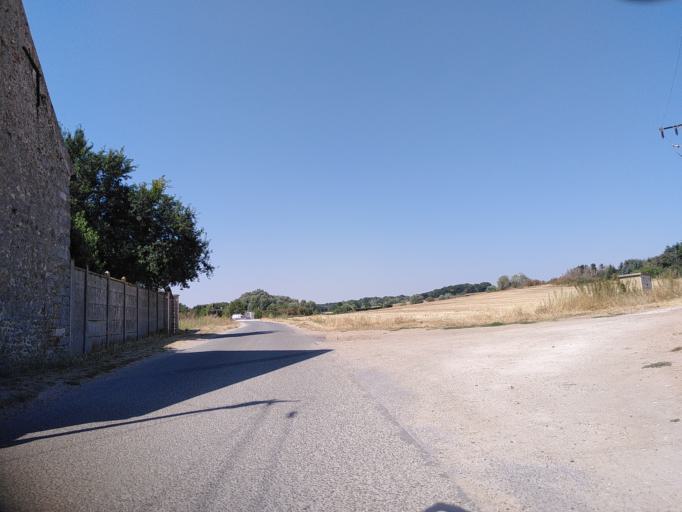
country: FR
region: Ile-de-France
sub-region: Departement de l'Essonne
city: Ollainville
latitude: 48.5847
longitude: 2.2089
